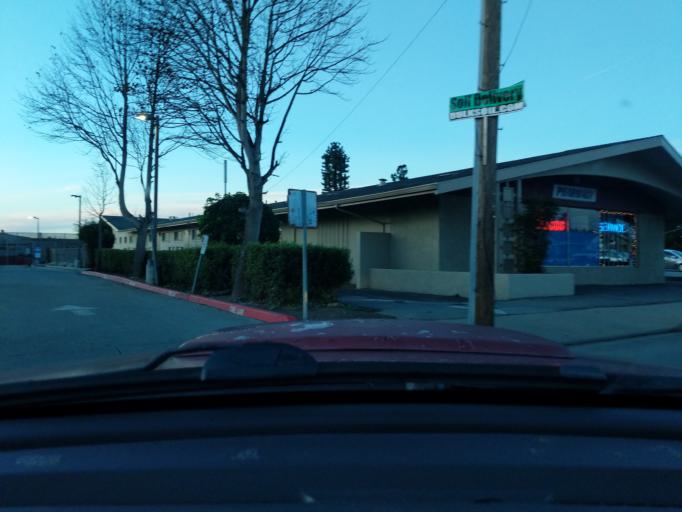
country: US
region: California
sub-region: Monterey County
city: Salinas
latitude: 36.6780
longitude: -121.6261
